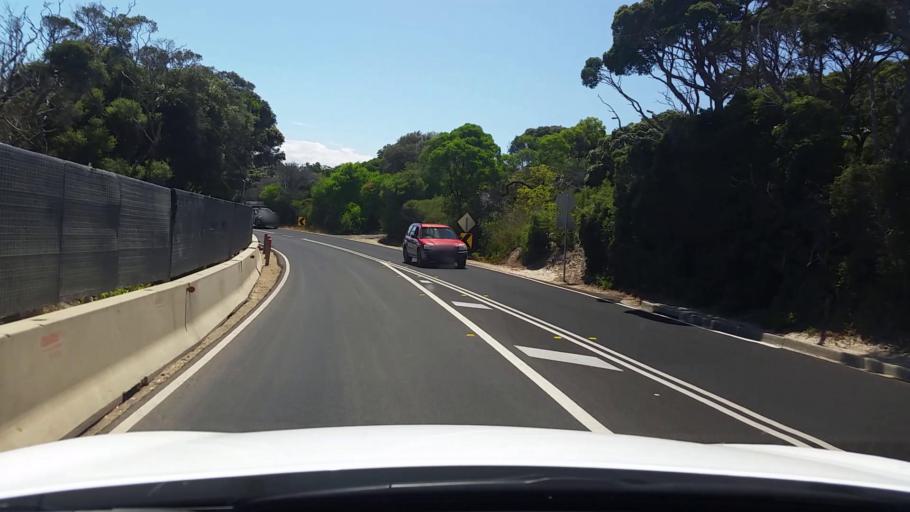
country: AU
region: Victoria
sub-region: Mornington Peninsula
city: Mount Martha
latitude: -38.2779
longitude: 145.0002
